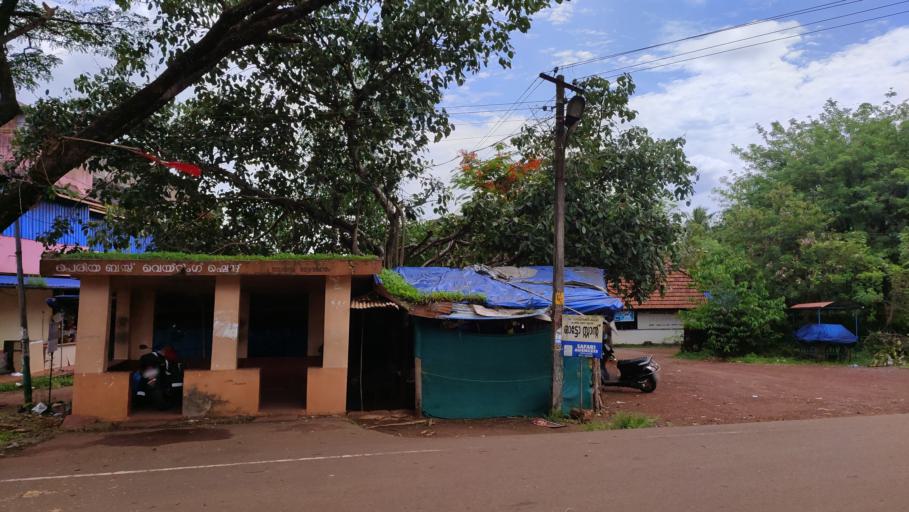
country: IN
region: Kerala
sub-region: Kasaragod District
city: Kannangad
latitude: 12.4020
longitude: 75.0970
